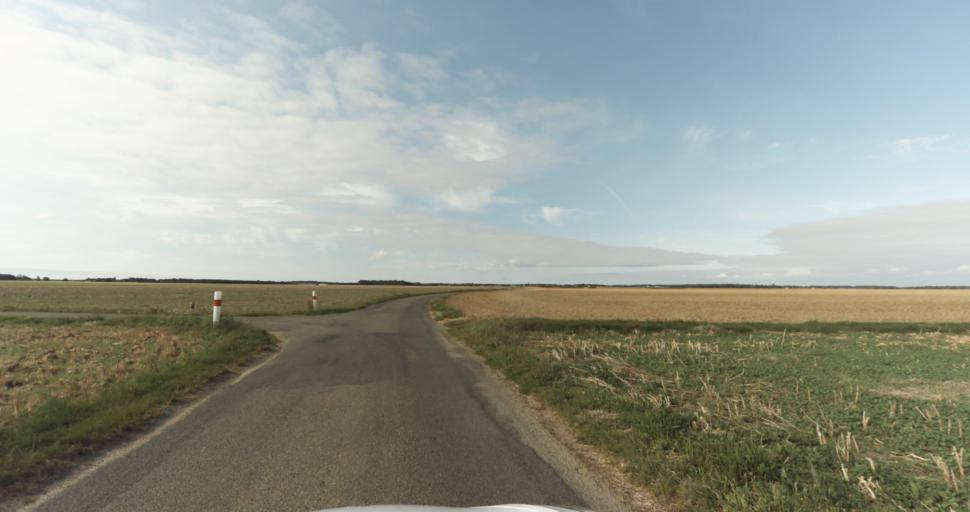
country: FR
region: Haute-Normandie
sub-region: Departement de l'Eure
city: Nonancourt
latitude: 48.8169
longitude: 1.1550
